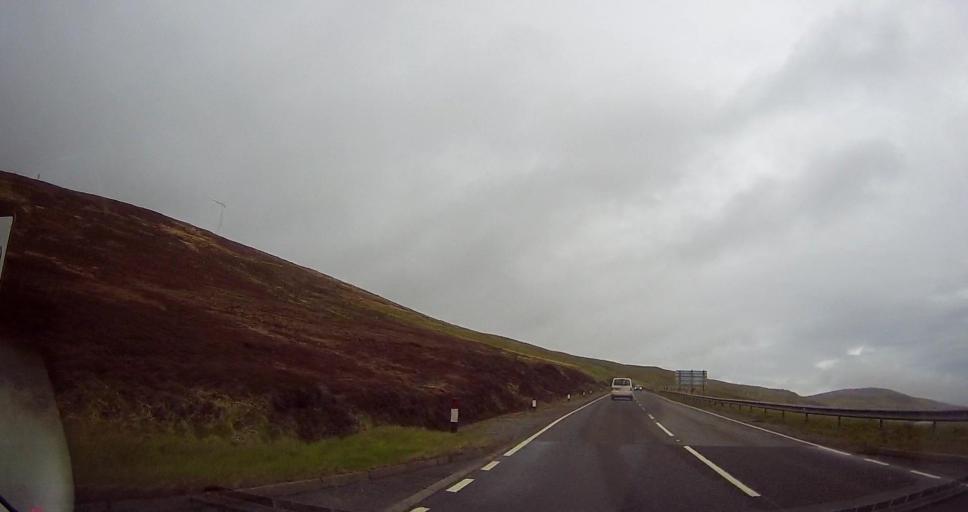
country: GB
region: Scotland
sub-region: Shetland Islands
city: Lerwick
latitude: 60.1611
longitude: -1.2267
